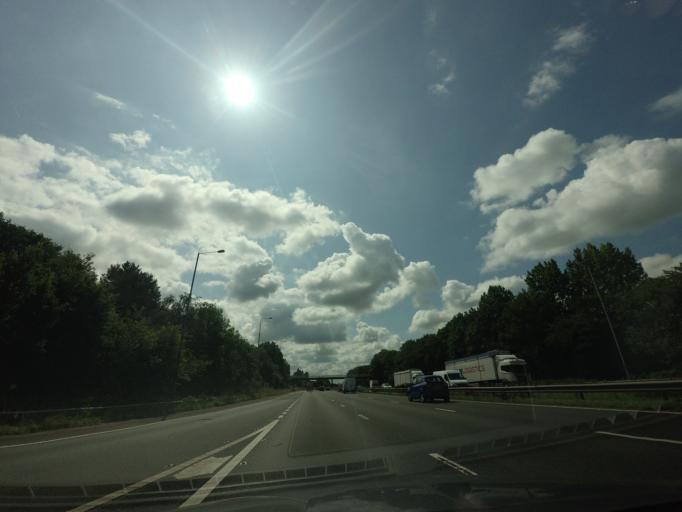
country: GB
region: England
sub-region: Lancashire
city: Clayton-le-Woods
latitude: 53.6933
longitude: -2.6774
